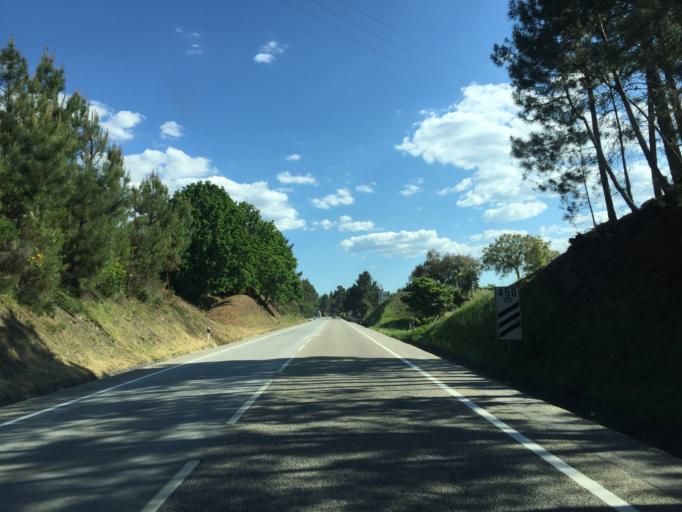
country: PT
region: Leiria
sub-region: Pedrogao Grande
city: Pedrogao Grande
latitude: 39.9155
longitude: -8.1537
